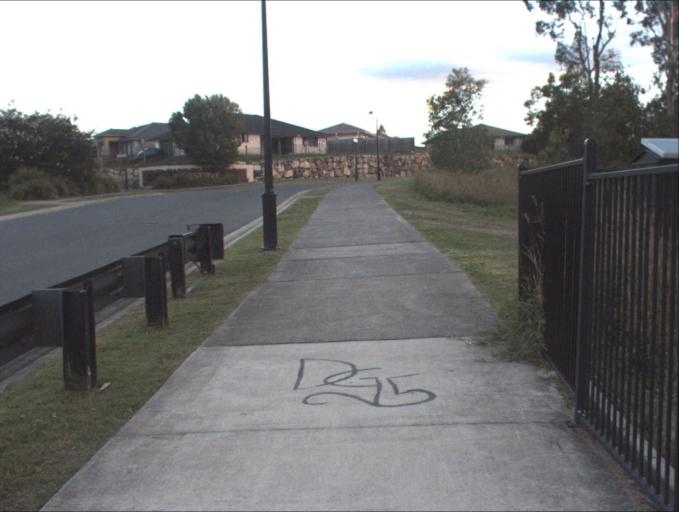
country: AU
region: Queensland
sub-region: Logan
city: North Maclean
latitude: -27.8015
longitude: 152.9574
